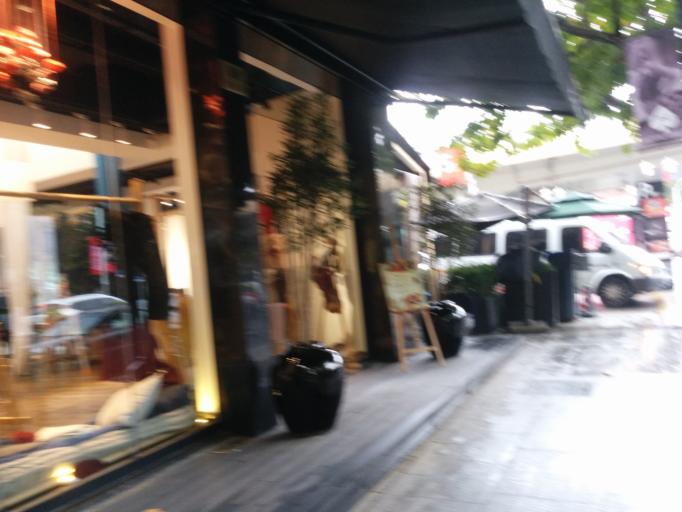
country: CN
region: Shanghai Shi
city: Shanghai
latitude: 31.2250
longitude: 121.4465
